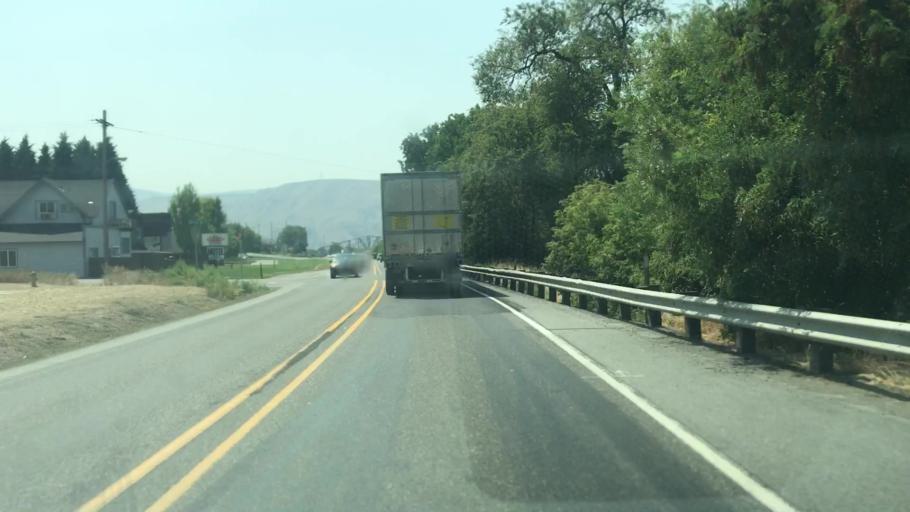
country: US
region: Washington
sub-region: Douglas County
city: East Wenatchee
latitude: 47.4247
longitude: -120.2978
